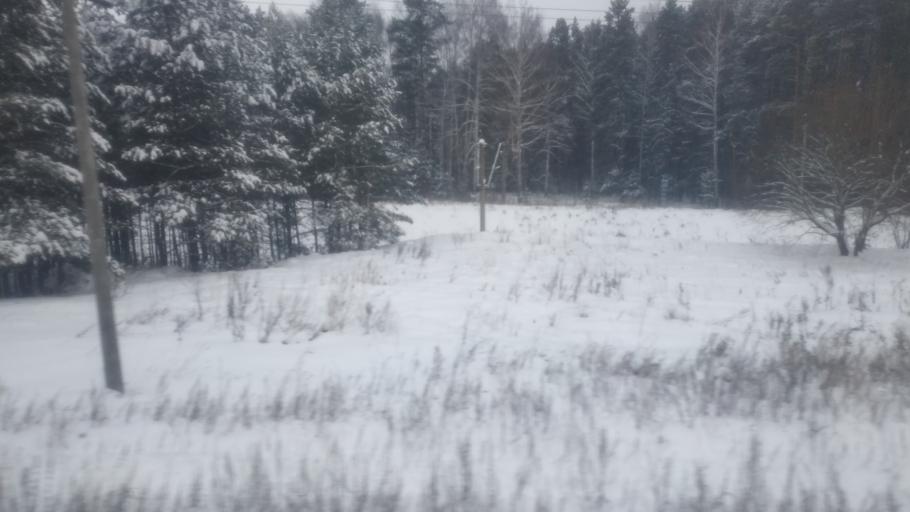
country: RU
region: Udmurtiya
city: Malaya Purga
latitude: 56.5531
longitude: 53.1004
